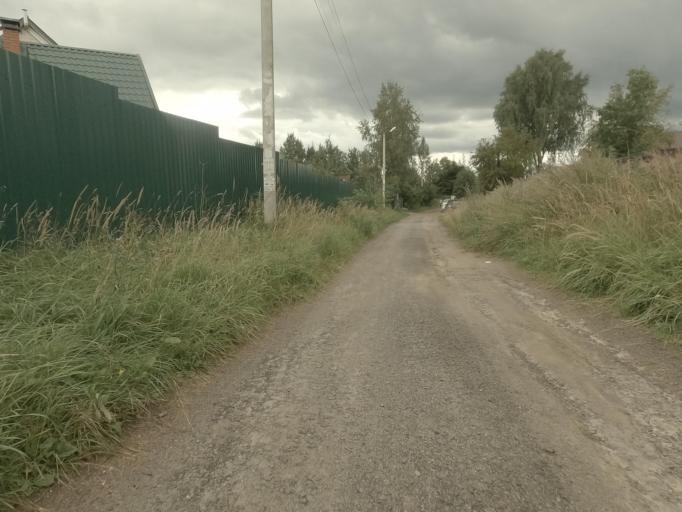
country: RU
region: Leningrad
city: Koltushi
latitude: 59.8880
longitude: 30.6952
